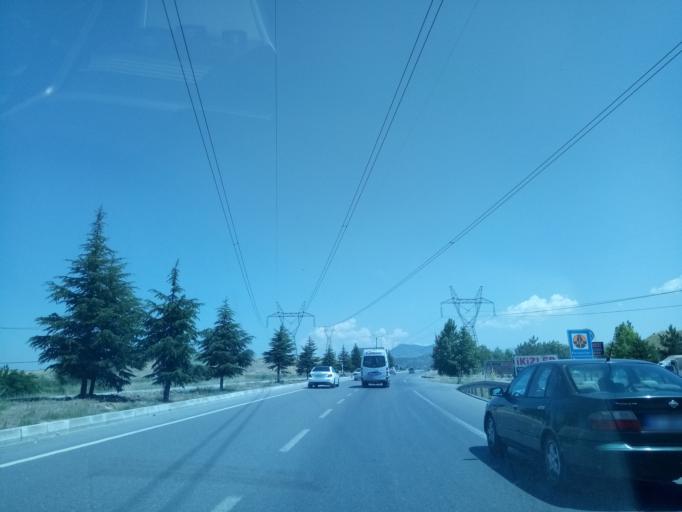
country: TR
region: Konya
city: Seydisehir
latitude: 37.4491
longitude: 31.8604
